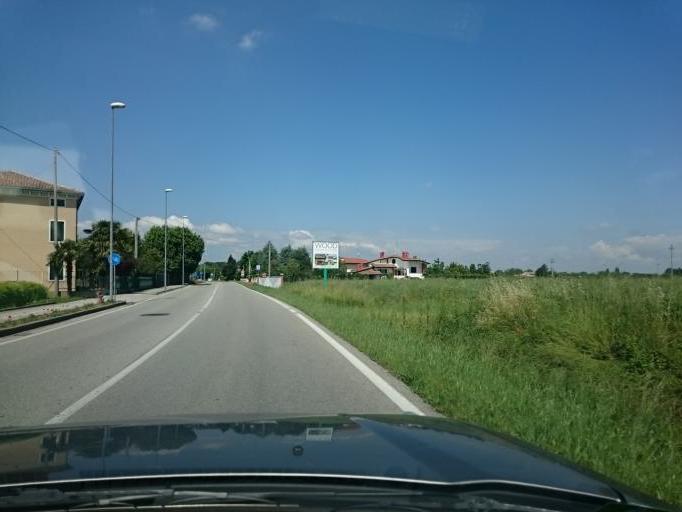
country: IT
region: Veneto
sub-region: Provincia di Padova
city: Saccolongo
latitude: 45.4109
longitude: 11.7324
